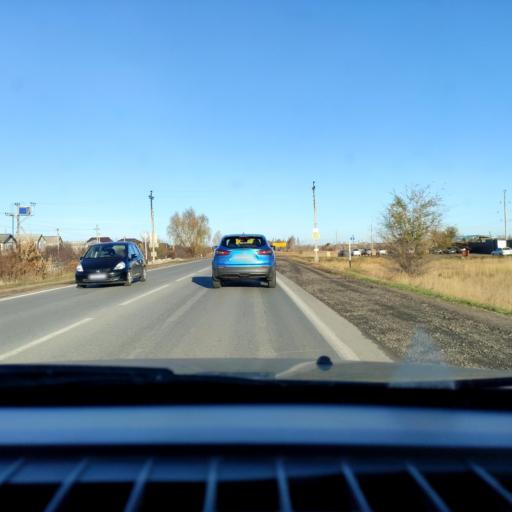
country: RU
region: Samara
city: Tol'yatti
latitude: 53.5759
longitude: 49.3388
